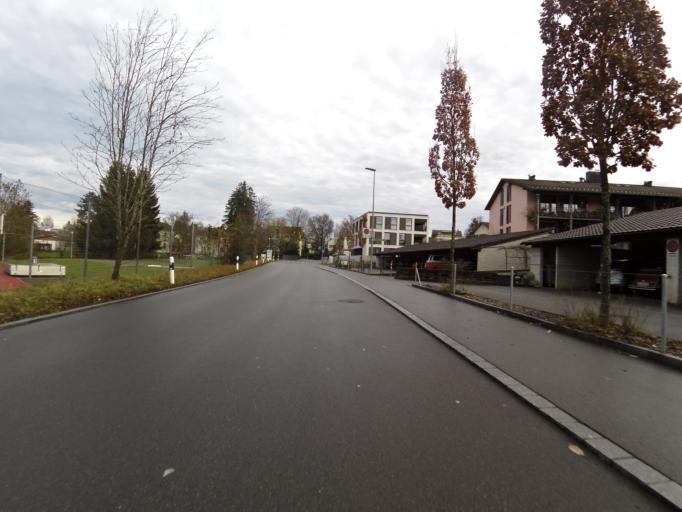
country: CH
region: Thurgau
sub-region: Frauenfeld District
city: Frauenfeld
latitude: 47.5517
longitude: 8.9012
